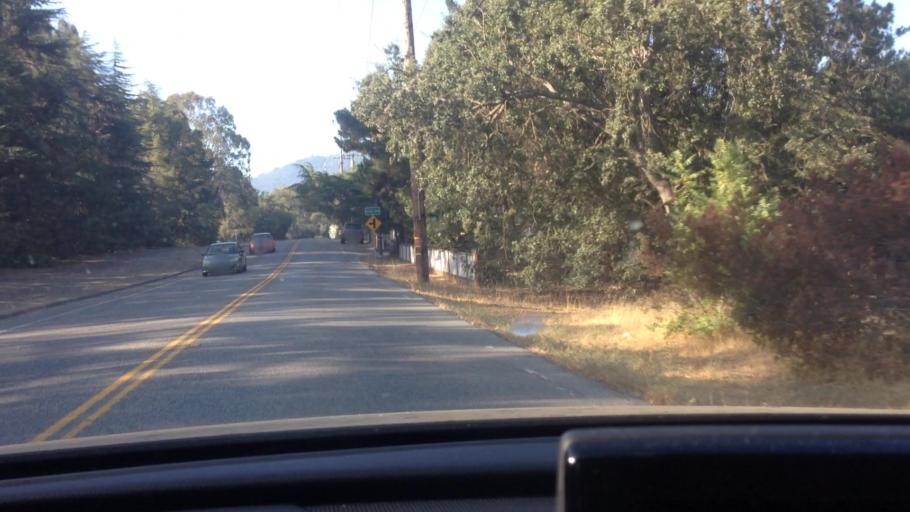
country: US
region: California
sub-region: Santa Clara County
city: Saratoga
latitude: 37.2537
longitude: -122.0138
